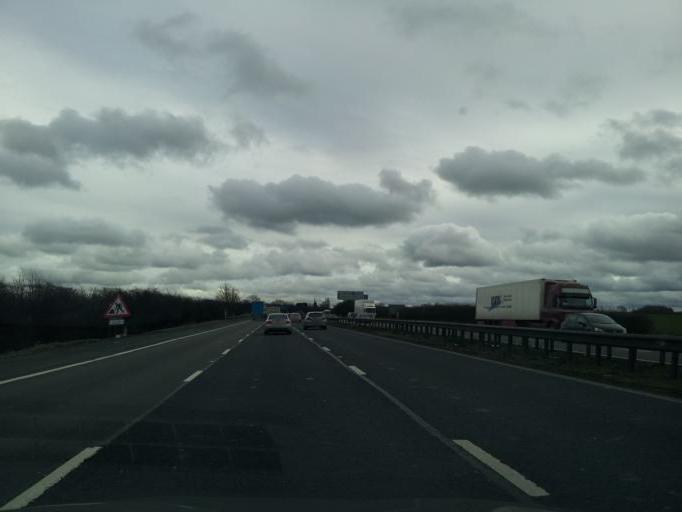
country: GB
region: England
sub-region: Staffordshire
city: Stone
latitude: 52.8935
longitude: -2.1786
